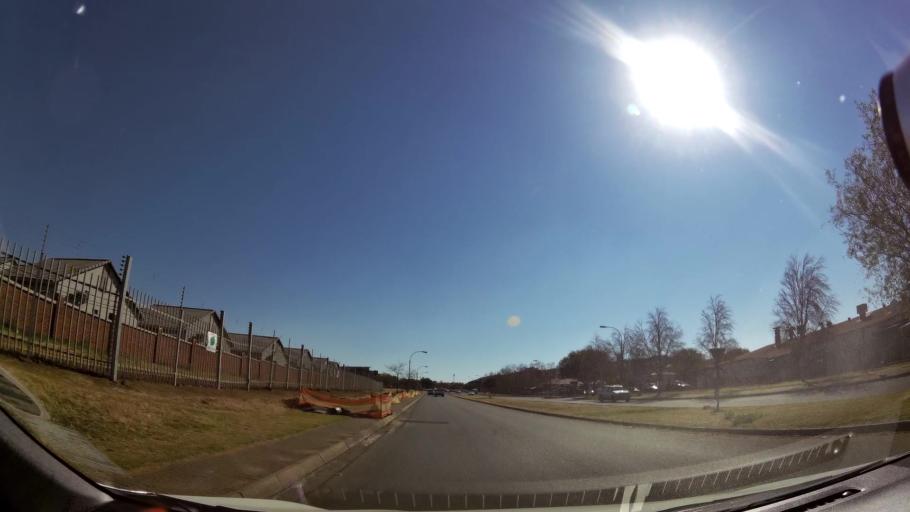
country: ZA
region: Gauteng
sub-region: City of Johannesburg Metropolitan Municipality
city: Johannesburg
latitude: -26.2915
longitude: 28.0905
